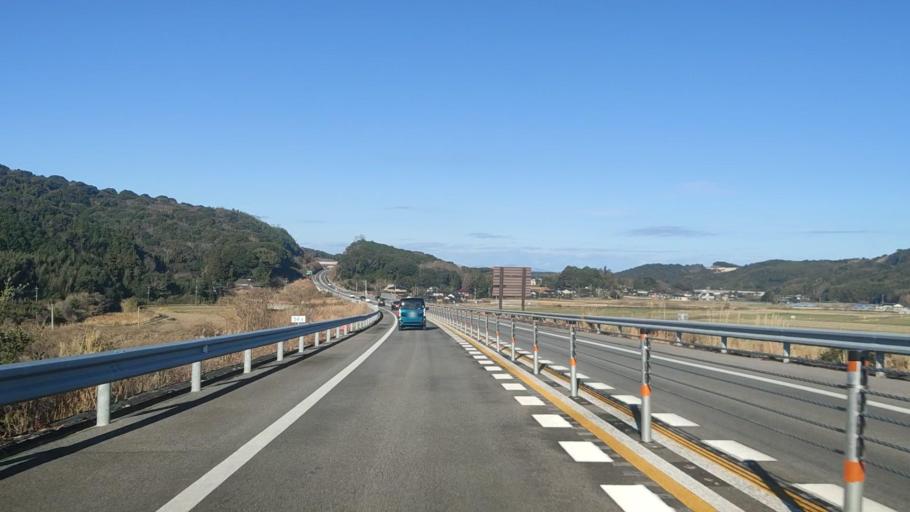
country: JP
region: Fukuoka
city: Nakatsu
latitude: 33.5232
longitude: 131.2513
